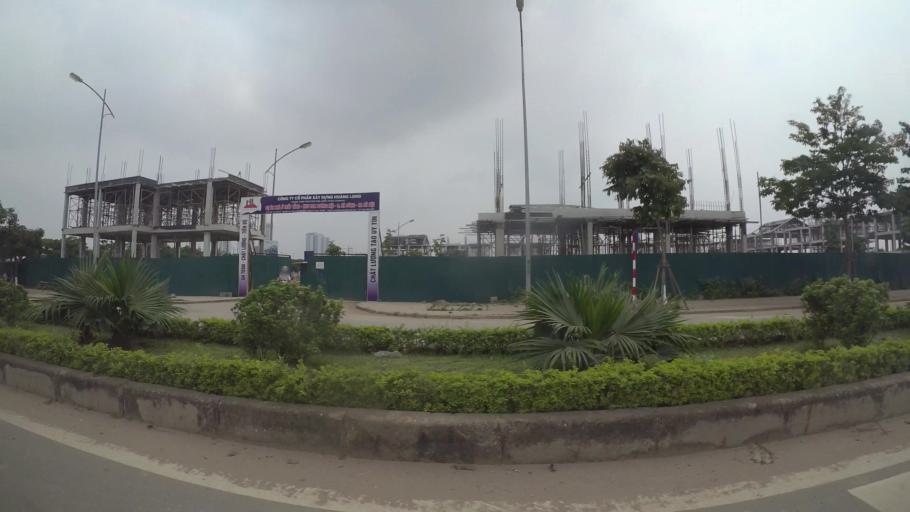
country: VN
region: Ha Noi
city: Ha Dong
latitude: 20.9826
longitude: 105.7549
